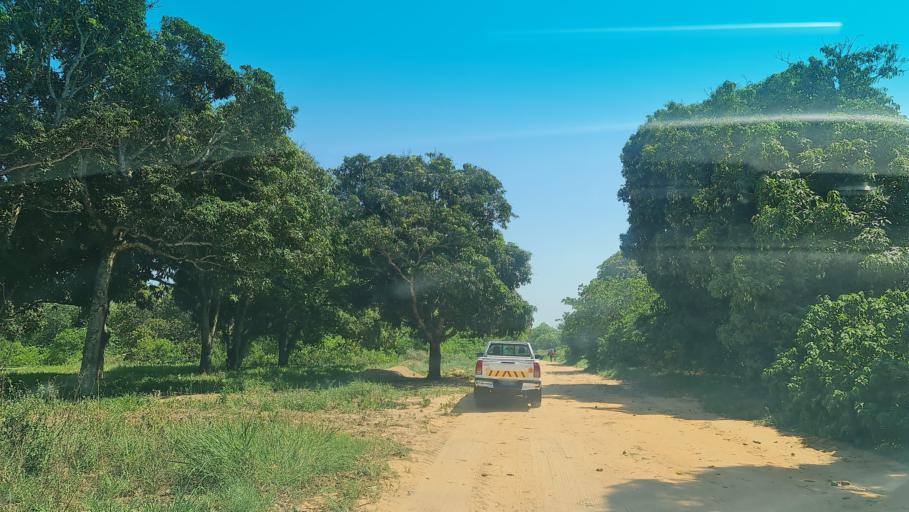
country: MZ
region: Gaza
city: Macia
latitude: -25.0770
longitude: 33.1017
